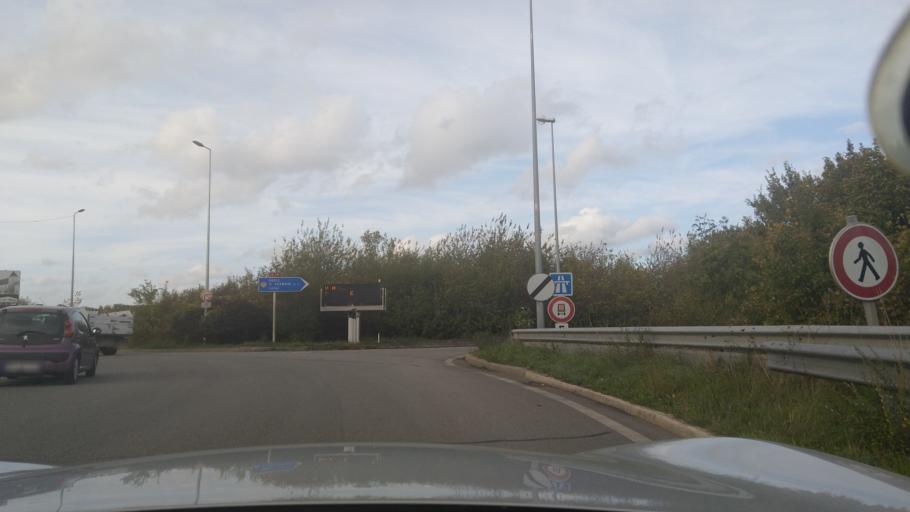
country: FR
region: Ile-de-France
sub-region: Departement des Yvelines
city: Chambourcy
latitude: 48.9174
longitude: 2.0127
